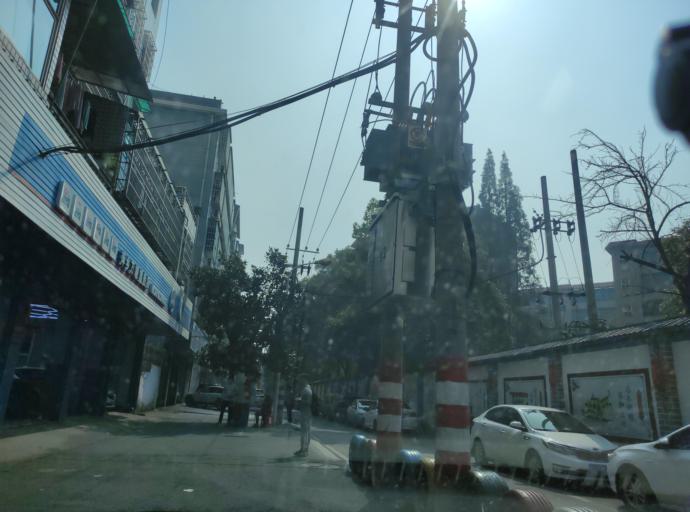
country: CN
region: Jiangxi Sheng
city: Pingxiang
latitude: 27.6361
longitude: 113.8538
